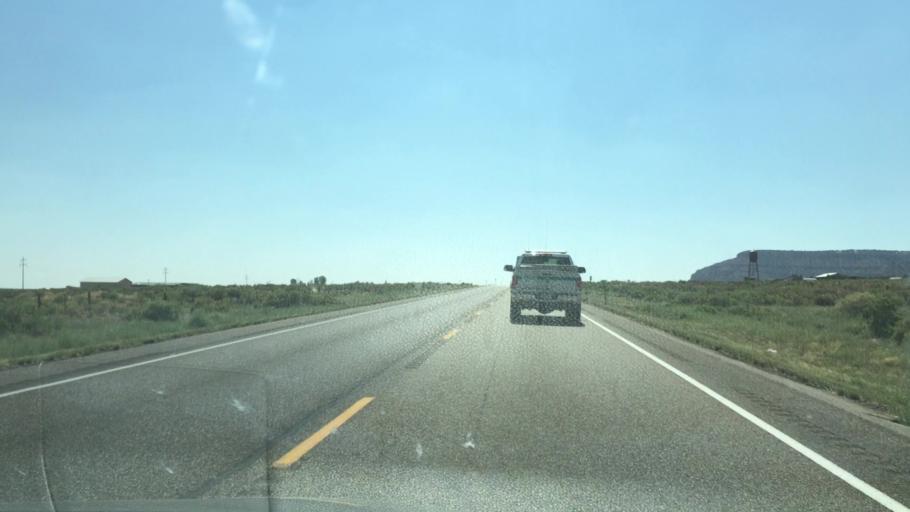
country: US
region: Utah
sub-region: Kane County
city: Kanab
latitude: 37.0332
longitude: -112.3901
